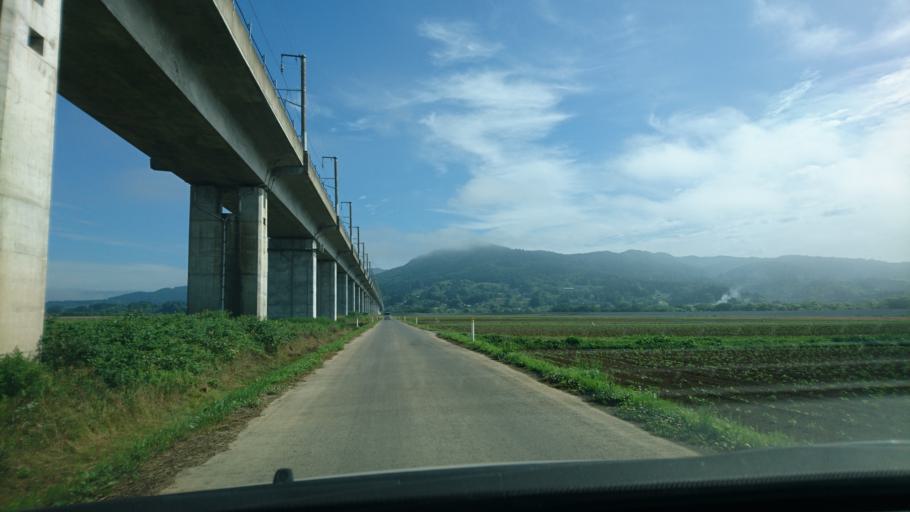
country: JP
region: Iwate
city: Ichinoseki
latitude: 38.9643
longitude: 141.1529
